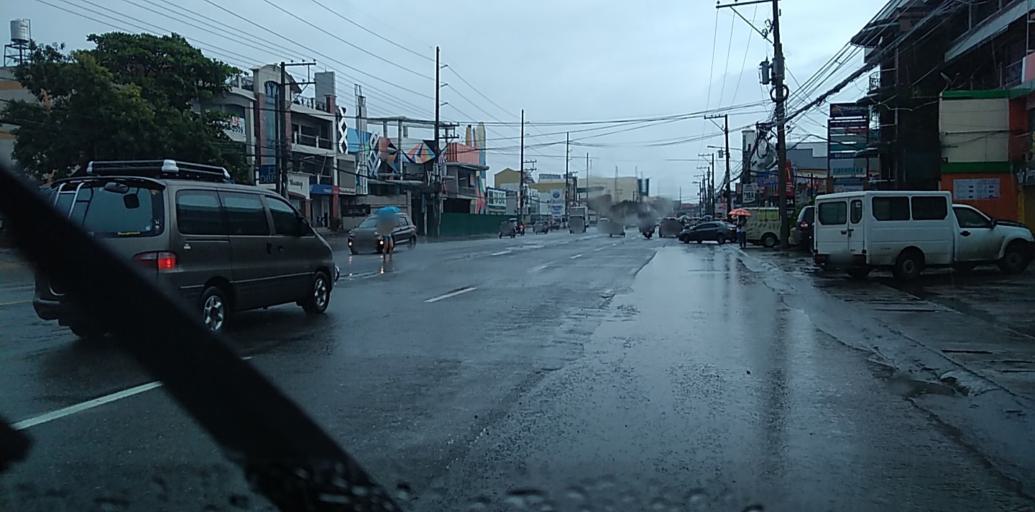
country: PH
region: Central Luzon
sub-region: Province of Pampanga
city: Magliman
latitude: 15.0416
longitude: 120.6771
